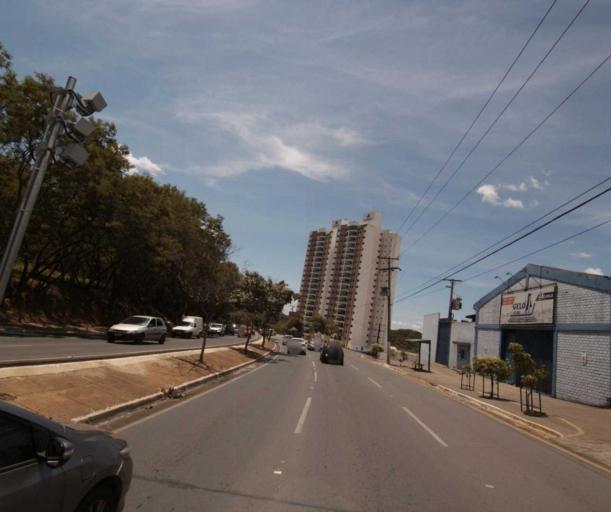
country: BR
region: Mato Grosso
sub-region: Cuiaba
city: Cuiaba
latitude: -15.5750
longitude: -56.1033
